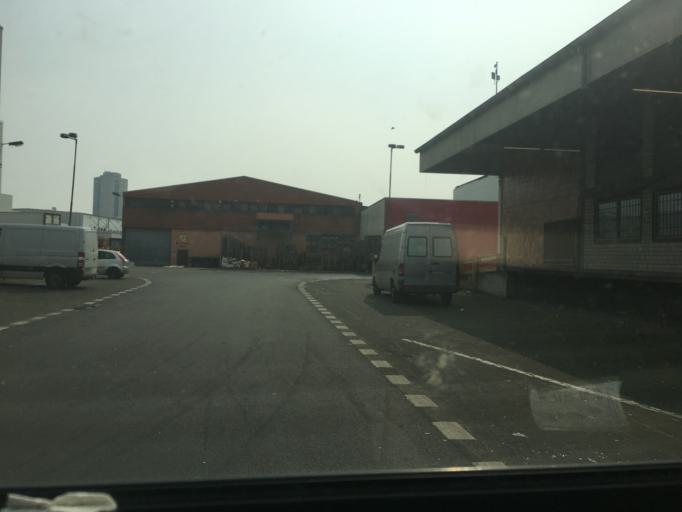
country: DE
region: North Rhine-Westphalia
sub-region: Regierungsbezirk Koln
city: Neustadt/Sued
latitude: 50.9140
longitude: 6.9541
